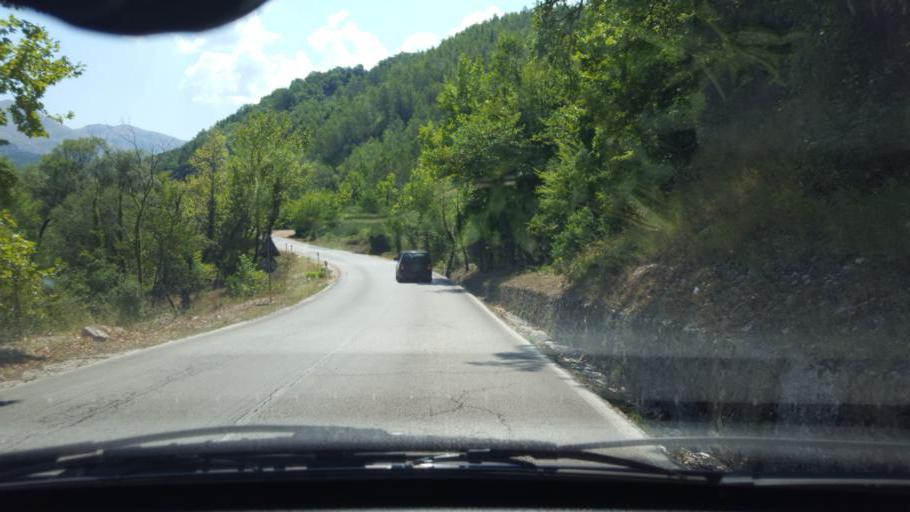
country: AL
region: Vlore
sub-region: Rrethi i Delvines
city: Delvine
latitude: 39.9218
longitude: 20.1646
